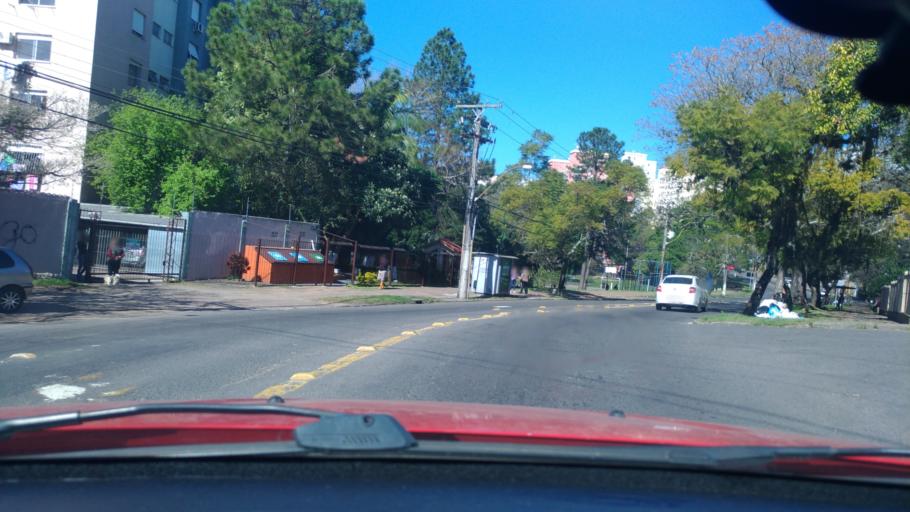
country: BR
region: Rio Grande do Sul
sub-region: Porto Alegre
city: Porto Alegre
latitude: -30.0374
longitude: -51.1441
